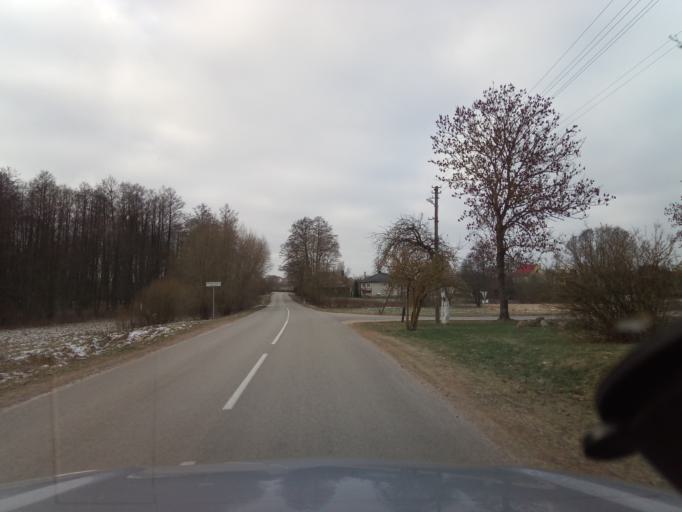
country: LT
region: Alytaus apskritis
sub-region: Alytaus rajonas
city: Daugai
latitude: 54.3575
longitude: 24.3374
